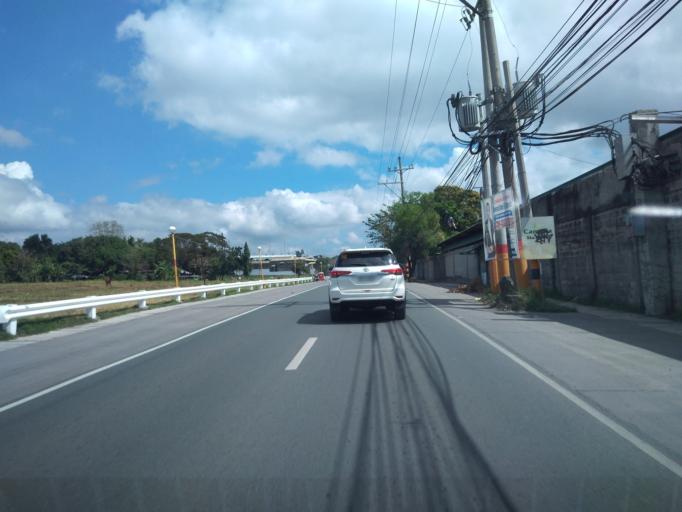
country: PH
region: Central Luzon
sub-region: Province of Bulacan
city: Santa Maria
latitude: 14.8279
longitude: 120.9711
